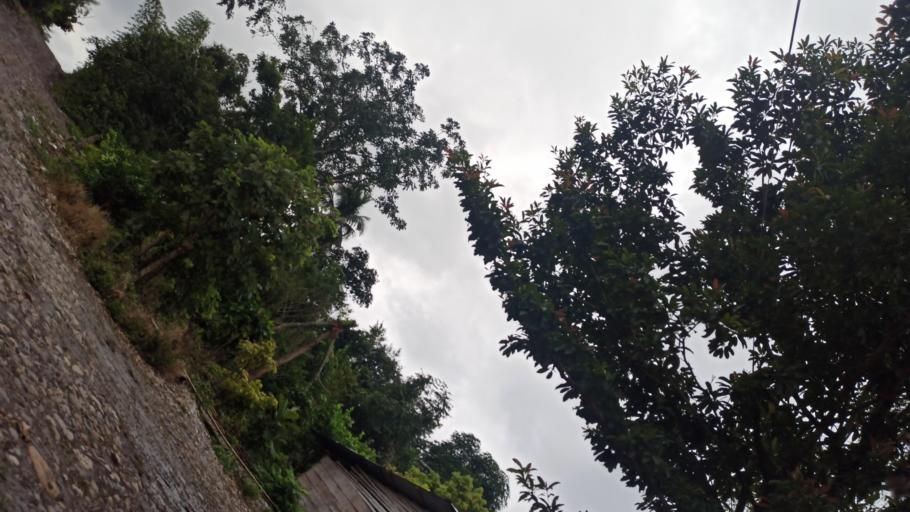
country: MX
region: Puebla
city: Espinal
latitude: 20.2896
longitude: -97.3921
